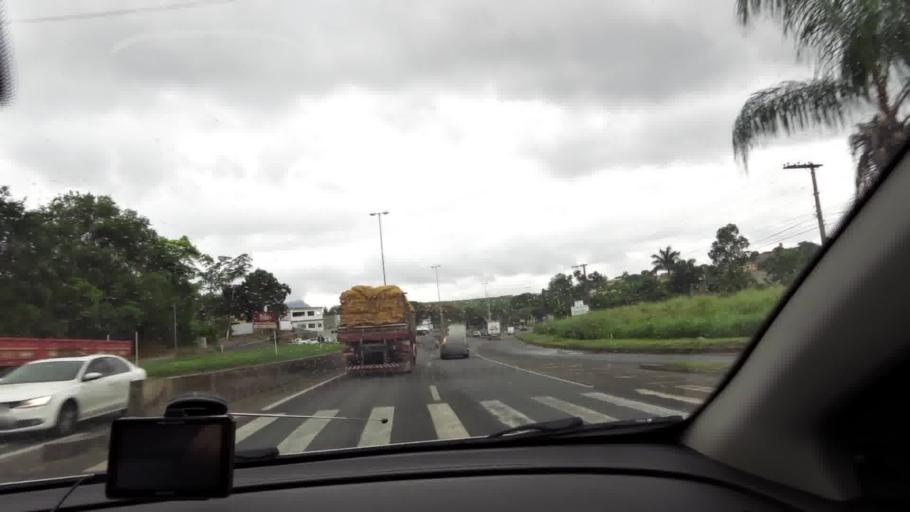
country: BR
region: Espirito Santo
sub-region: Viana
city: Viana
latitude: -20.3641
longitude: -40.4431
